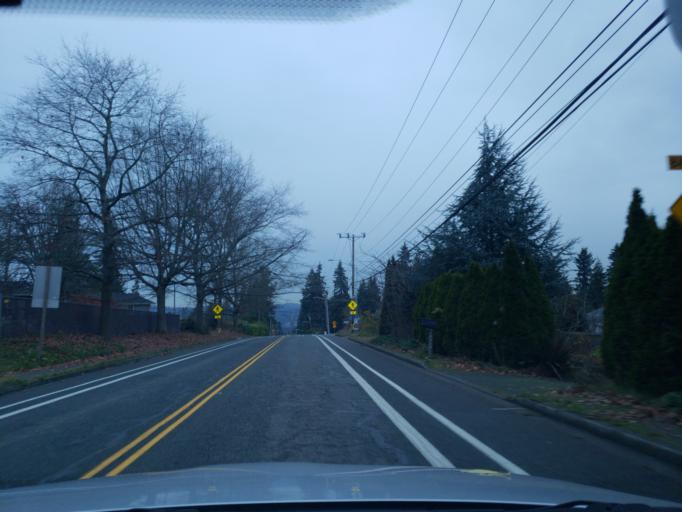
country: US
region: Washington
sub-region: King County
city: Kenmore
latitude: 47.7441
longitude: -122.2278
